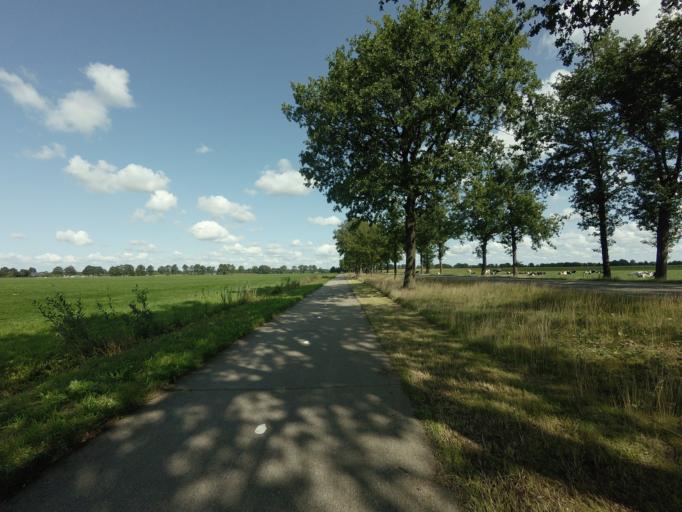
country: NL
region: Overijssel
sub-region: Gemeente Dalfsen
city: Dalfsen
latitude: 52.5517
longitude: 6.2618
